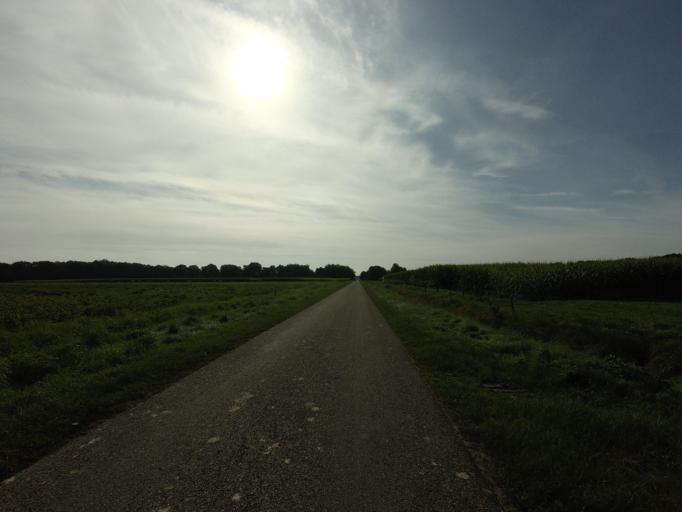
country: NL
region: Drenthe
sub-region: Gemeente Aa en Hunze
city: Anloo
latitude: 52.9423
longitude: 6.6752
